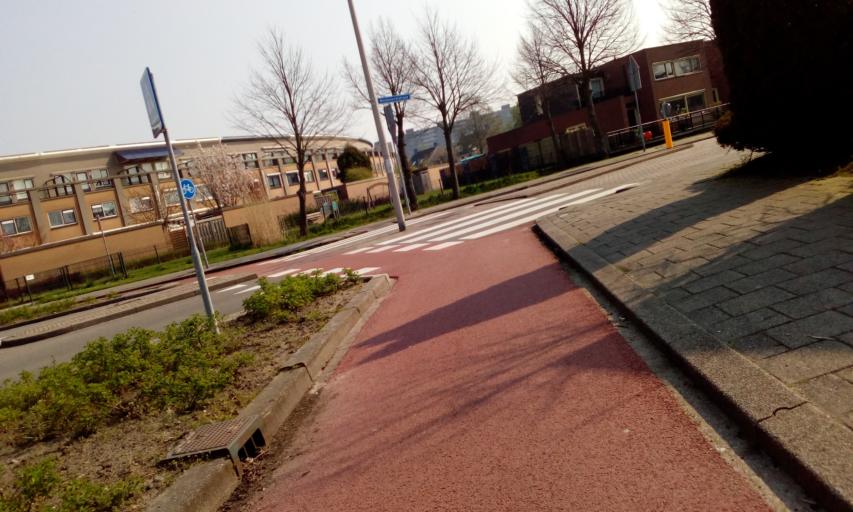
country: NL
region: South Holland
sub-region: Gemeente Capelle aan den IJssel
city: Capelle-West
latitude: 51.9196
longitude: 4.5666
